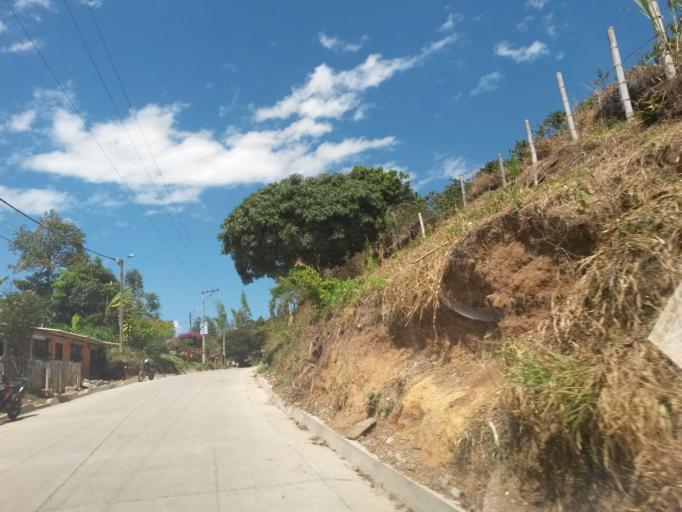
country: CO
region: Cauca
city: Morales
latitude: 2.7523
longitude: -76.6310
